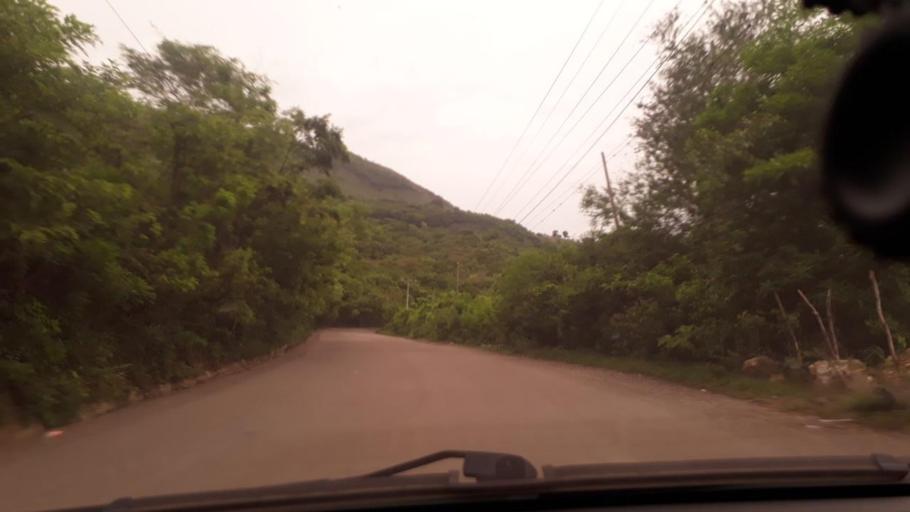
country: GT
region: Chiquimula
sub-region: Municipio de San Juan Ermita
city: San Juan Ermita
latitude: 14.7524
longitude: -89.4499
